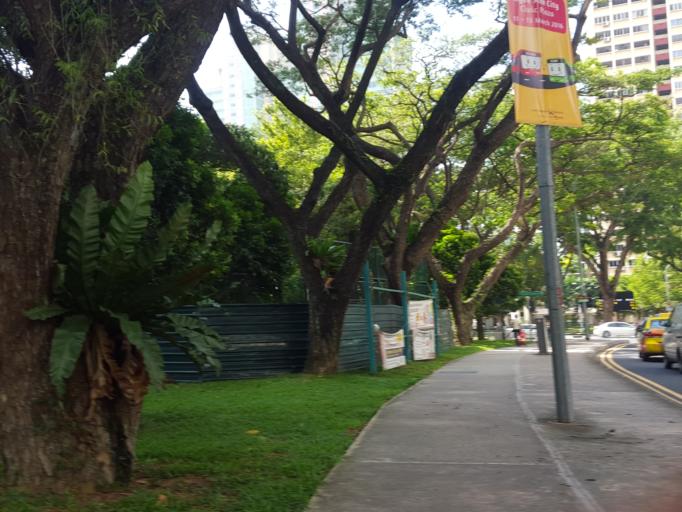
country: SG
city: Singapore
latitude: 1.3350
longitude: 103.8469
